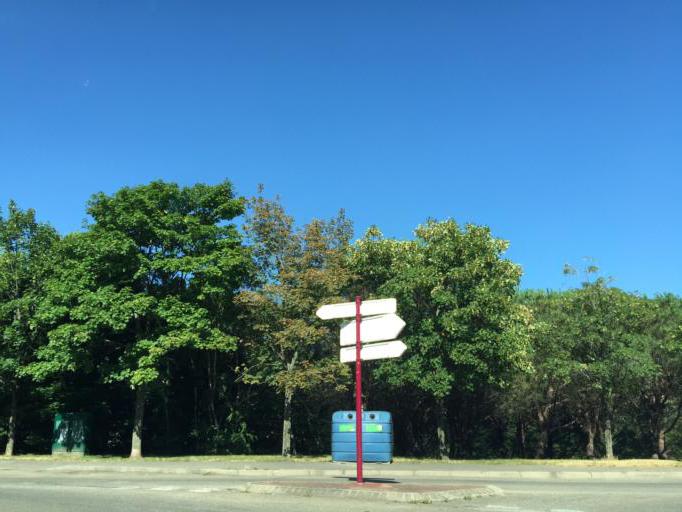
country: FR
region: Rhone-Alpes
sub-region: Departement de la Loire
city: Saint-Chamond
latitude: 45.4772
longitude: 4.5367
